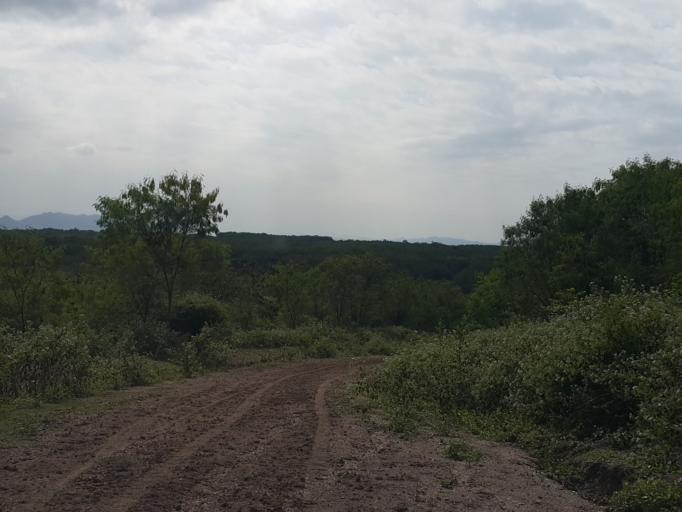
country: TH
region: Lampang
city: Mae Mo
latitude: 18.3413
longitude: 99.7656
